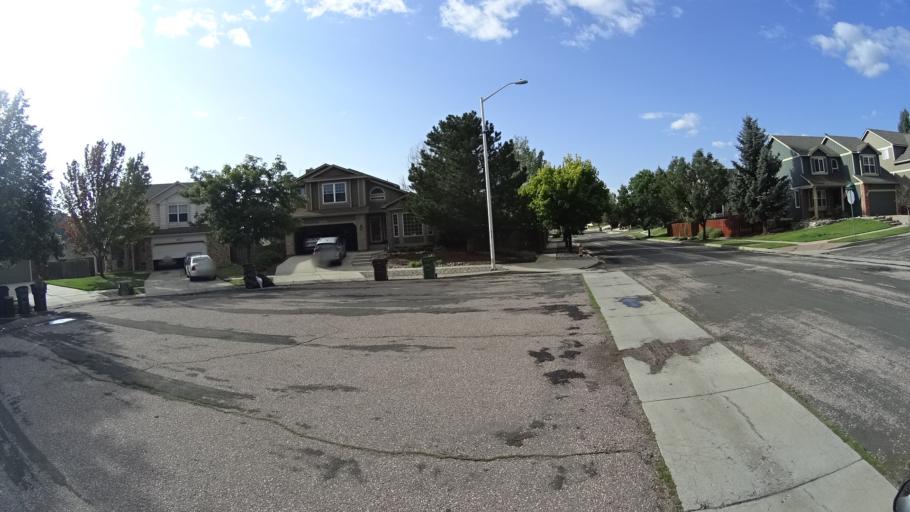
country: US
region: Colorado
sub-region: El Paso County
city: Manitou Springs
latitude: 38.9129
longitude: -104.8619
